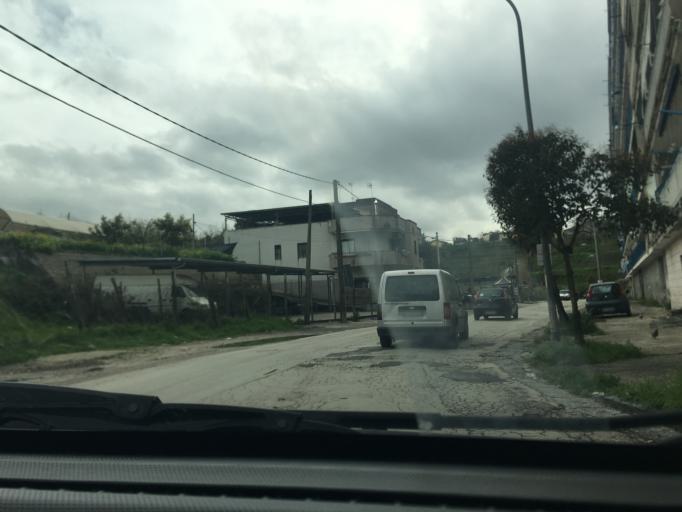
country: IT
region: Campania
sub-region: Provincia di Napoli
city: Mugnano di Napoli
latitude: 40.8956
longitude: 14.2029
